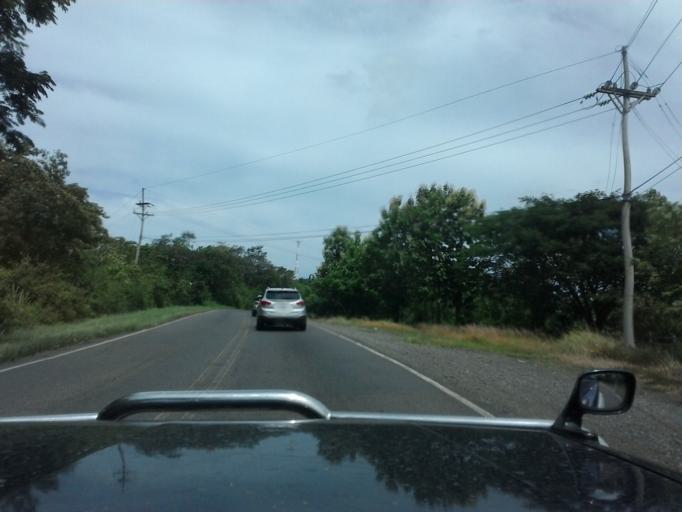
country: CR
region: Puntarenas
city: Esparza
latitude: 10.0199
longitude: -84.6062
